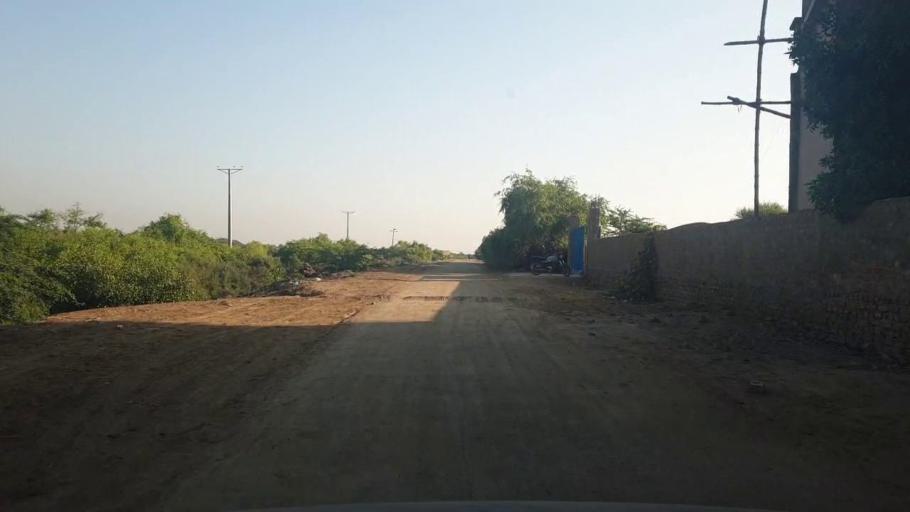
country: PK
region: Sindh
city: Badin
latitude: 24.7151
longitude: 68.8571
